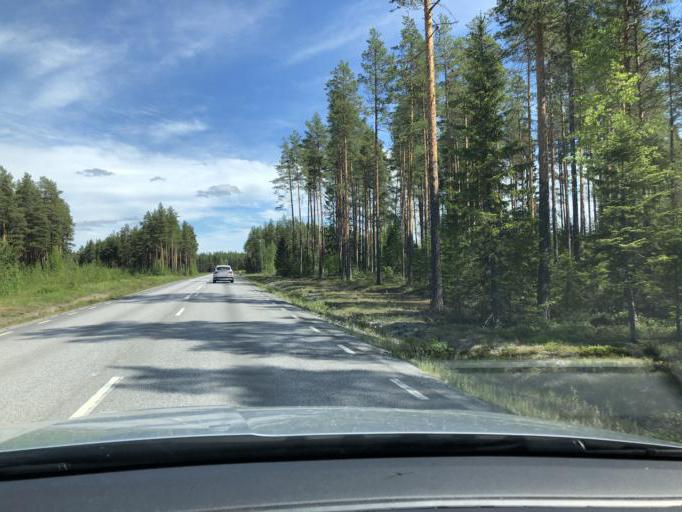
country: SE
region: Norrbotten
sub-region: Pitea Kommun
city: Roknas
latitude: 65.5208
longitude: 21.2007
